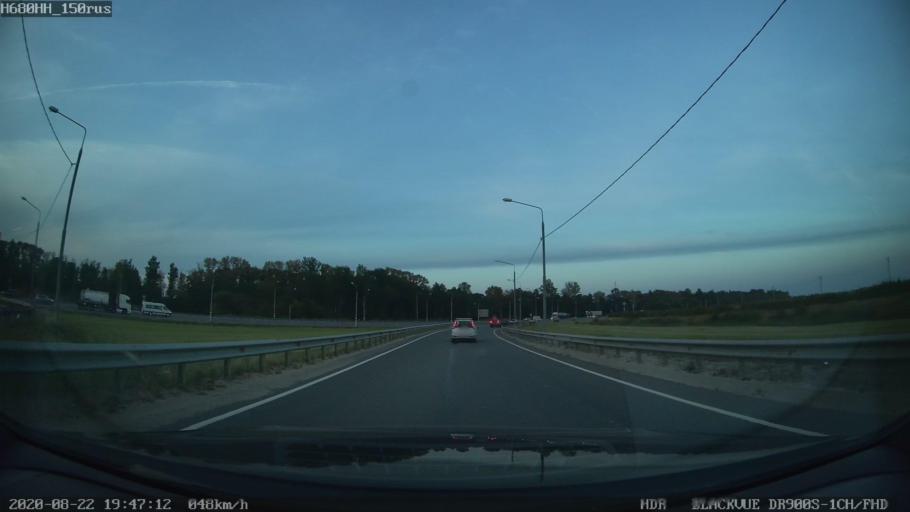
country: RU
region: Tverskaya
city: Emmaus
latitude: 56.7823
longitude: 36.0919
